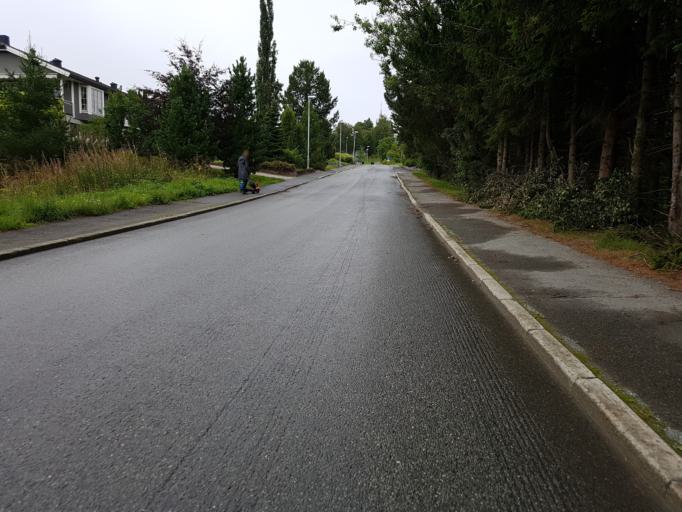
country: NO
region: Sor-Trondelag
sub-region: Trondheim
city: Trondheim
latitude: 63.4022
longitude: 10.3728
